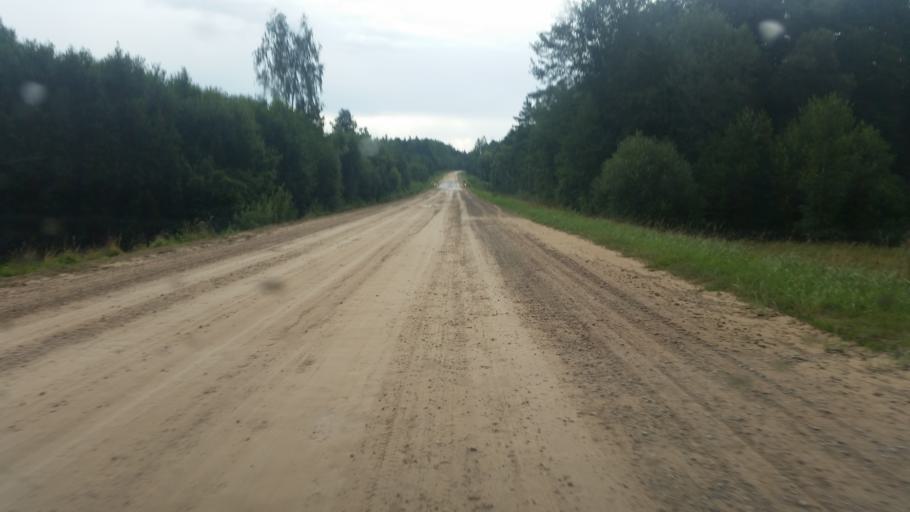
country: LV
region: Vecumnieki
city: Vecumnieki
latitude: 56.4421
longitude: 24.5730
